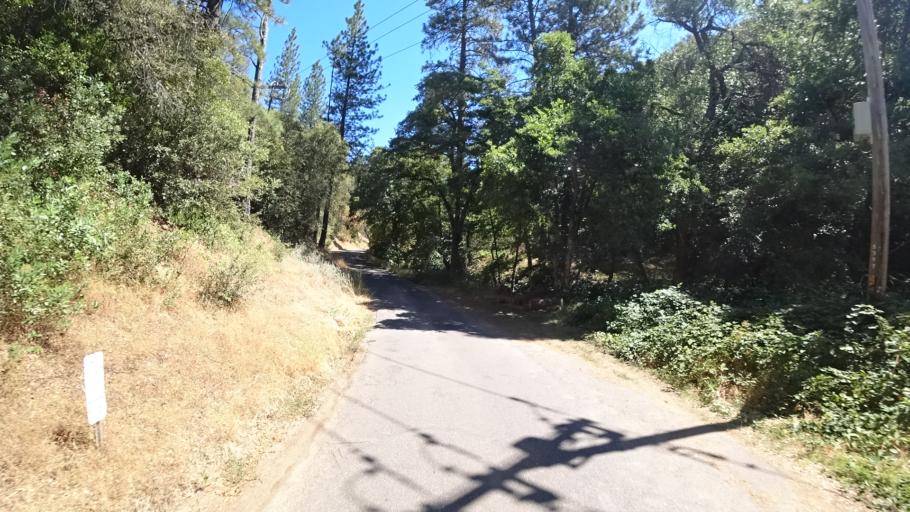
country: US
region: California
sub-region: Calaveras County
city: Murphys
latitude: 38.1478
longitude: -120.4462
